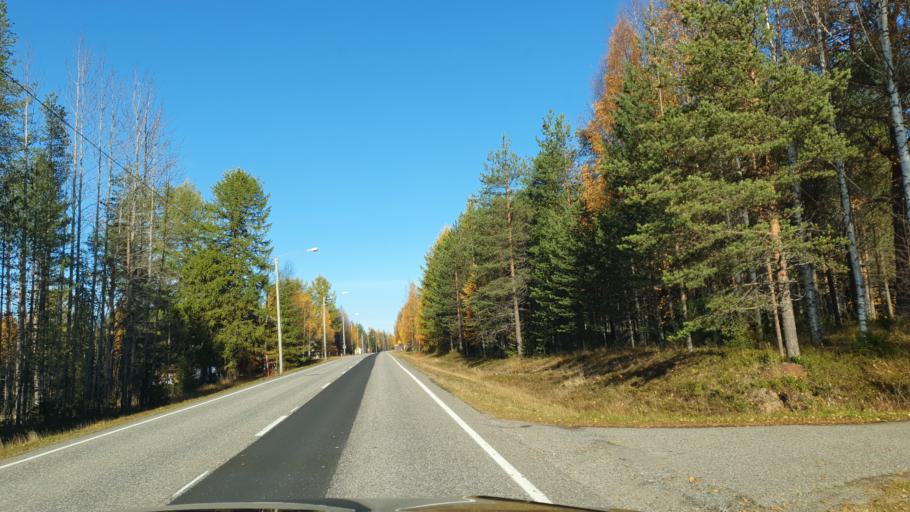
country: FI
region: Lapland
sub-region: Tunturi-Lappi
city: Kittilae
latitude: 67.3506
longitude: 24.8933
